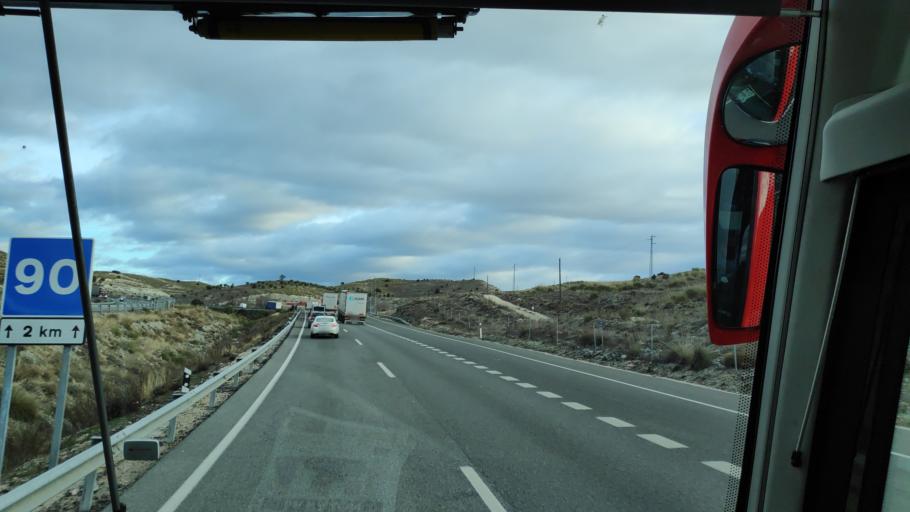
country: ES
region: Madrid
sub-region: Provincia de Madrid
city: Perales de Tajuna
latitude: 40.2098
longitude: -3.3229
